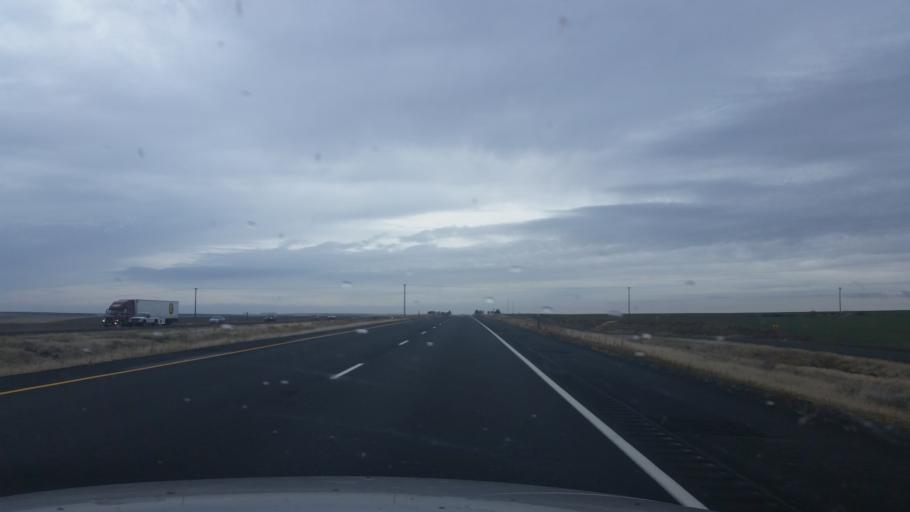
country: US
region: Washington
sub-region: Grant County
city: Warden
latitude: 47.0863
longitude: -118.8071
